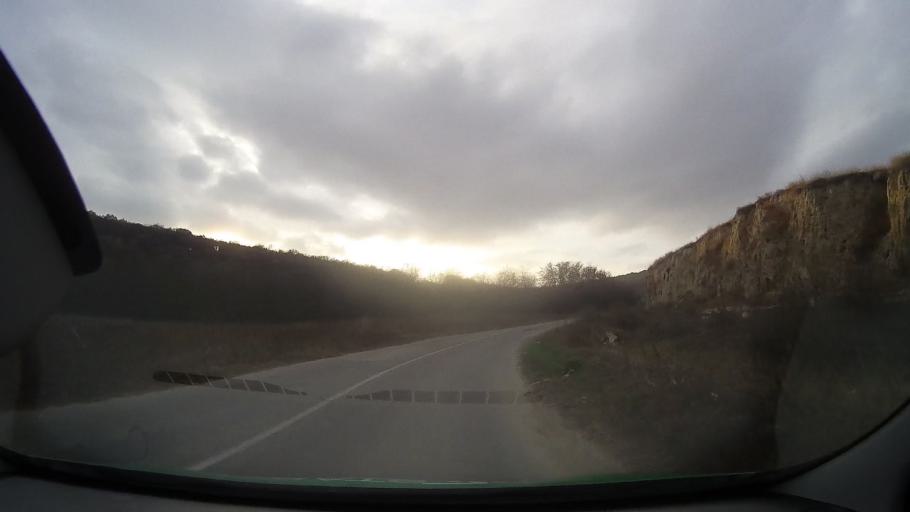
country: RO
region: Constanta
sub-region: Comuna Adamclisi
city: Adamclisi
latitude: 44.0387
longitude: 27.9507
